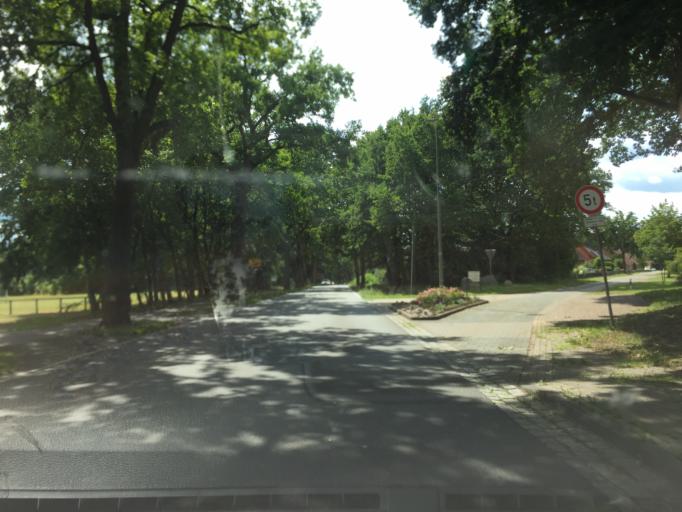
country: DE
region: Lower Saxony
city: Bohme
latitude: 52.8189
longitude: 9.4501
